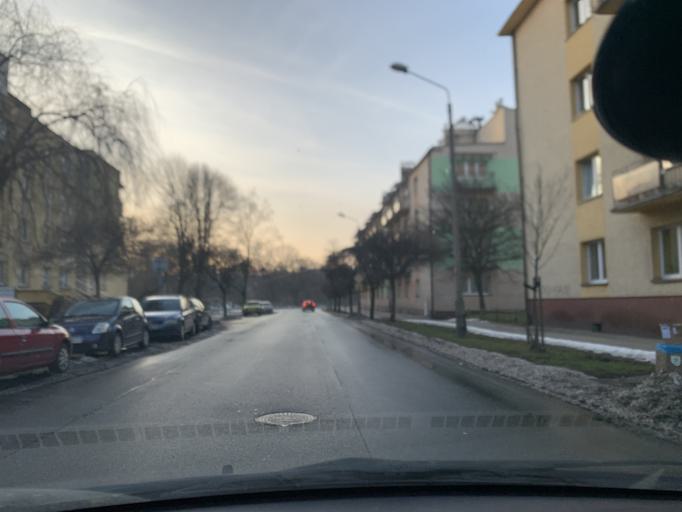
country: PL
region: Silesian Voivodeship
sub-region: Bytom
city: Bytom
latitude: 50.3542
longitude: 18.9090
